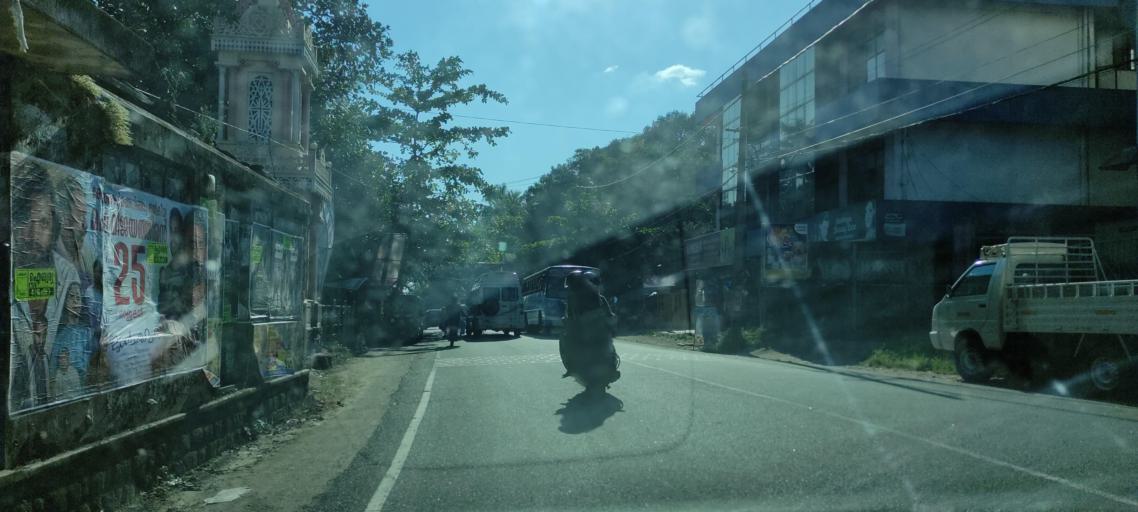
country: IN
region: Kerala
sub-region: Pattanamtitta
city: Pathanamthitta
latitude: 9.2554
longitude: 76.7630
